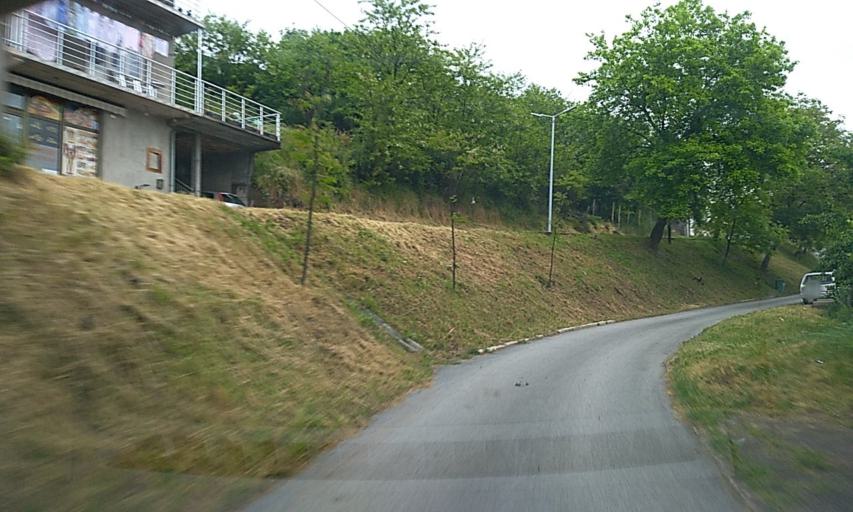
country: RS
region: Central Serbia
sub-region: Pcinjski Okrug
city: Vladicin Han
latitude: 42.7108
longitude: 22.0592
